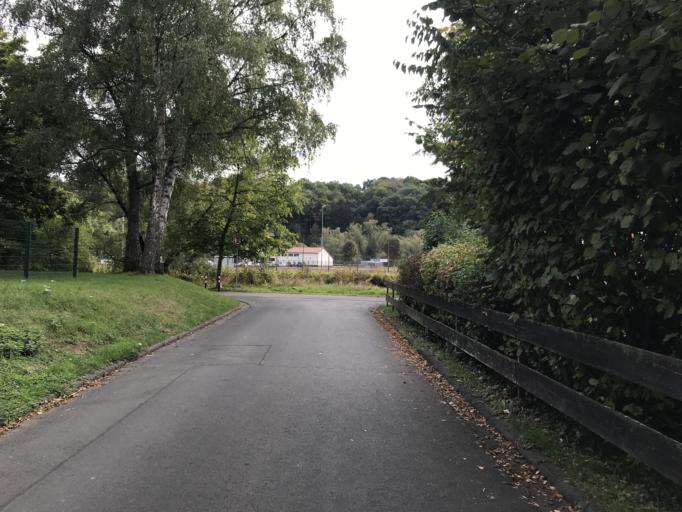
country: DE
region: Hesse
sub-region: Regierungsbezirk Giessen
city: Ehringshausen
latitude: 50.5955
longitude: 8.4155
